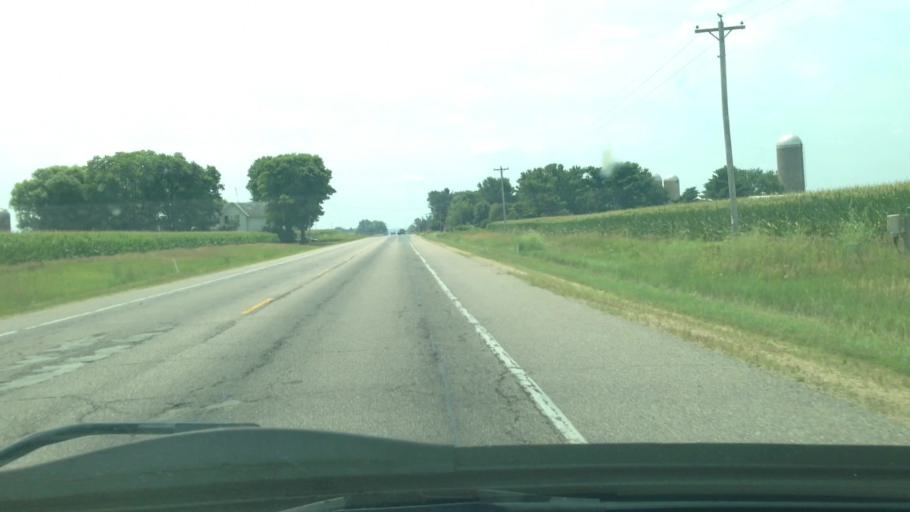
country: US
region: Wisconsin
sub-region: Sauk County
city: Prairie du Sac
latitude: 43.3061
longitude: -89.7592
